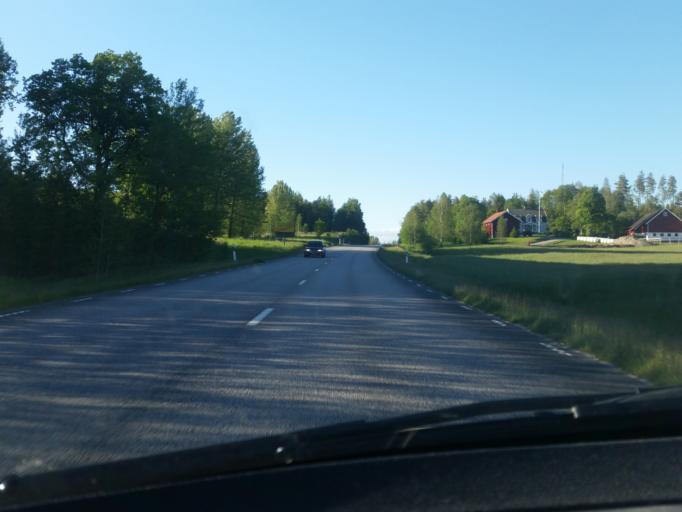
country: SE
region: Vaestra Goetaland
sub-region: Fargelanda Kommun
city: Faergelanda
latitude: 58.5550
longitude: 11.9935
